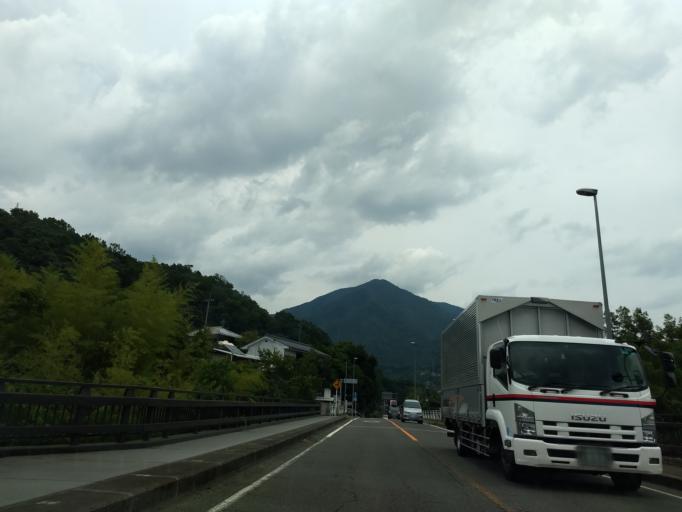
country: JP
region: Yamanashi
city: Otsuki
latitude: 35.6153
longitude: 138.9813
